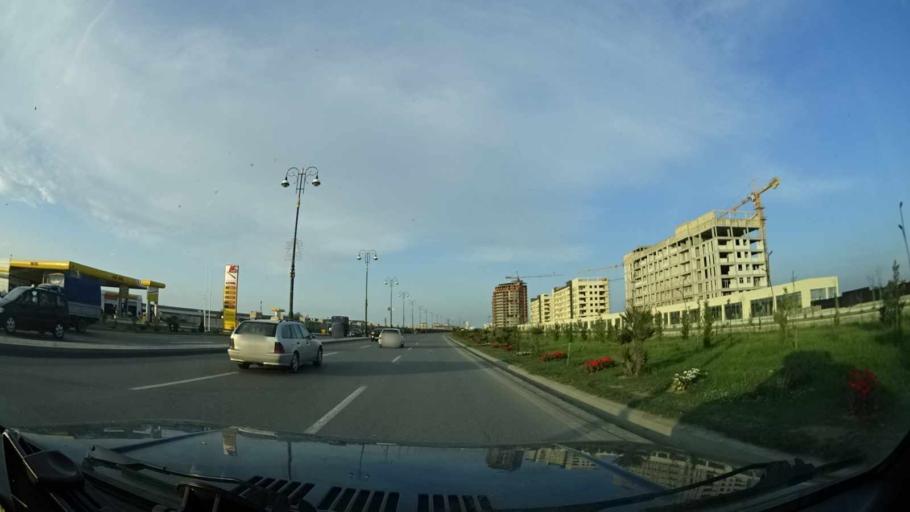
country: AZ
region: Sumqayit
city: Sumqayit
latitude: 40.5734
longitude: 49.6384
